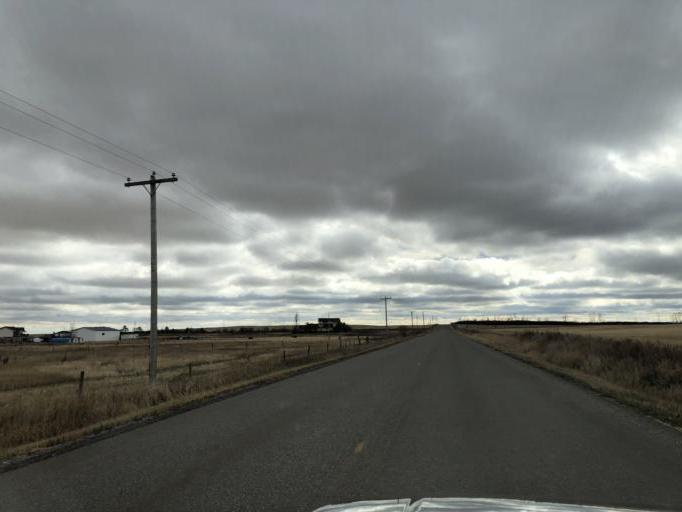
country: CA
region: Alberta
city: Chestermere
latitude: 50.9187
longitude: -113.8830
